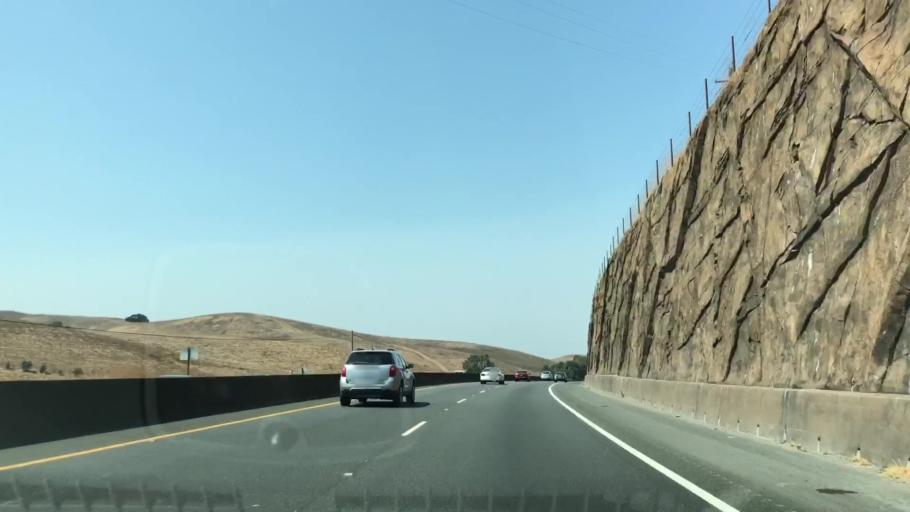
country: US
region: California
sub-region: Solano County
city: Green Valley
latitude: 38.2090
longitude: -122.1996
